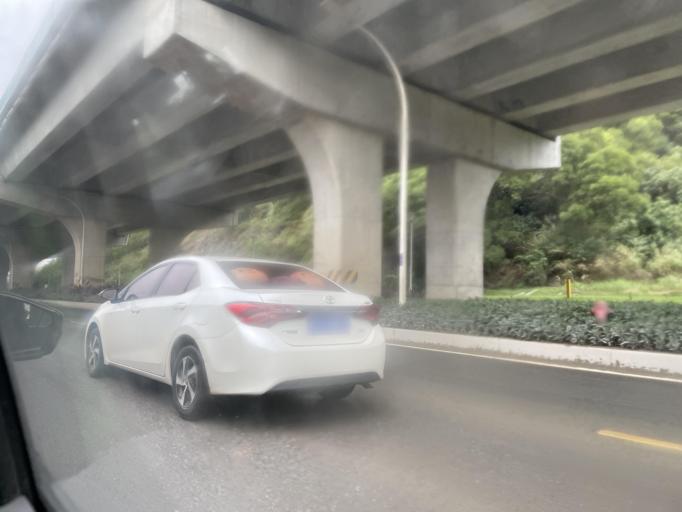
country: CN
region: Guangdong
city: Nanping
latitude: 22.1764
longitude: 113.4700
